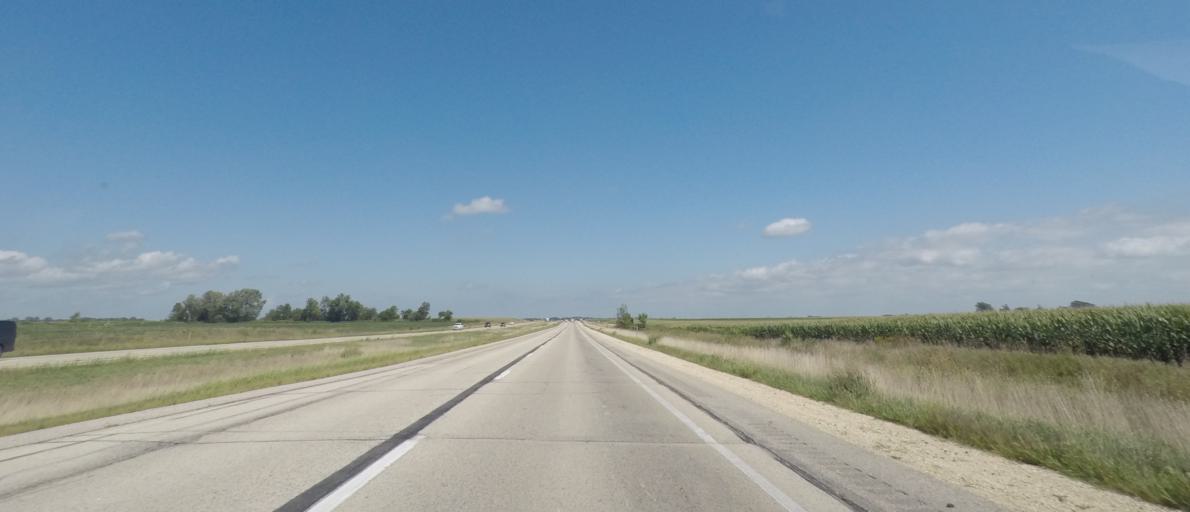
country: US
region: Iowa
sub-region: Linn County
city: Springville
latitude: 42.0678
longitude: -91.3794
